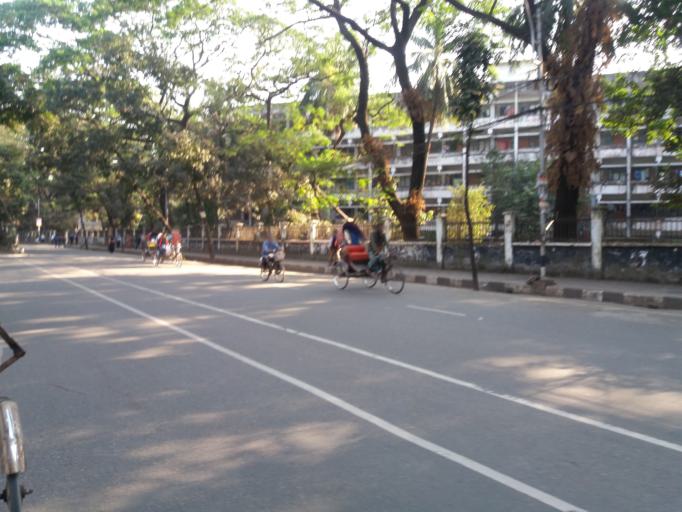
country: BD
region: Dhaka
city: Azimpur
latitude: 23.7266
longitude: 90.3905
